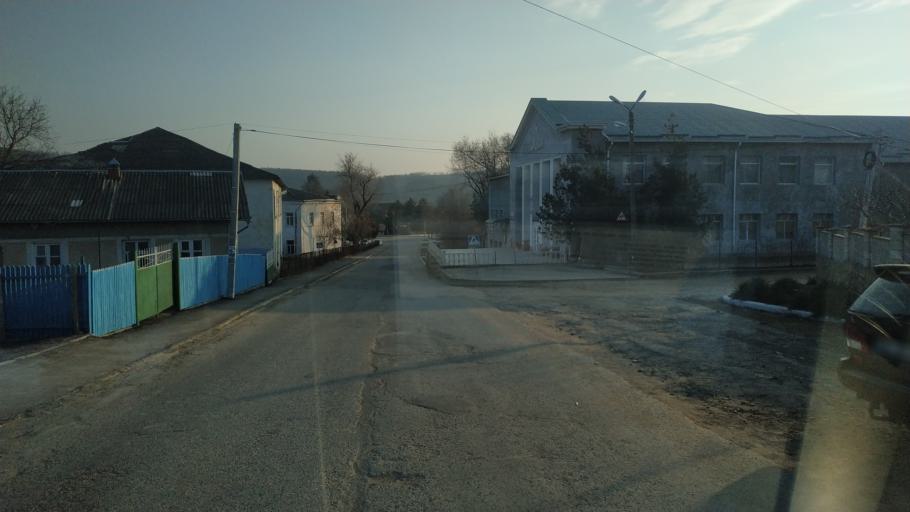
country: MD
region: Hincesti
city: Dancu
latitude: 46.7640
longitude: 28.3591
